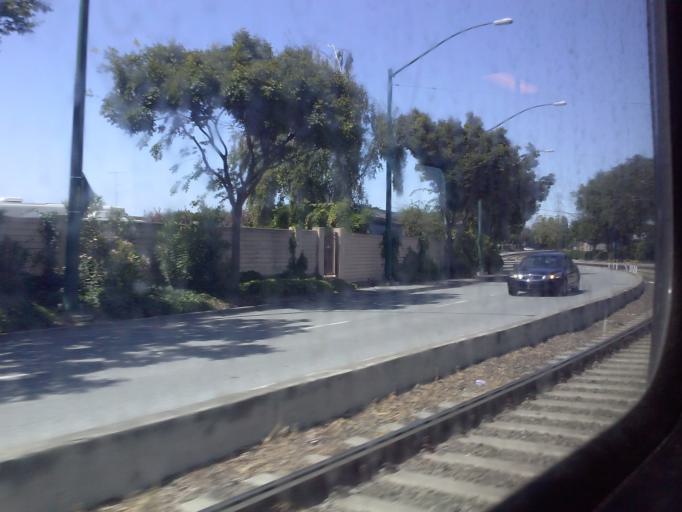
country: US
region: California
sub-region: Santa Clara County
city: Sunnyvale
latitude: 37.4033
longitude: -122.0045
